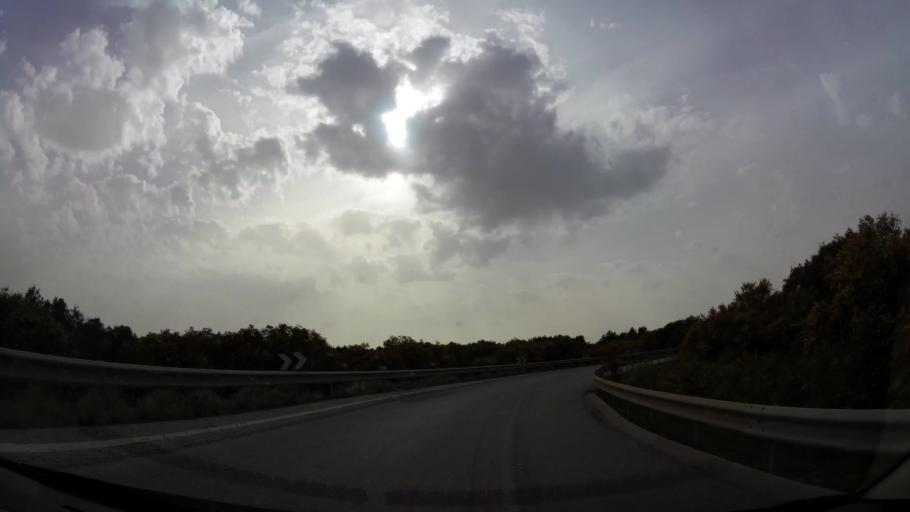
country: MA
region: Tanger-Tetouan
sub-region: Tanger-Assilah
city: Boukhalef
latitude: 35.6718
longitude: -5.9370
